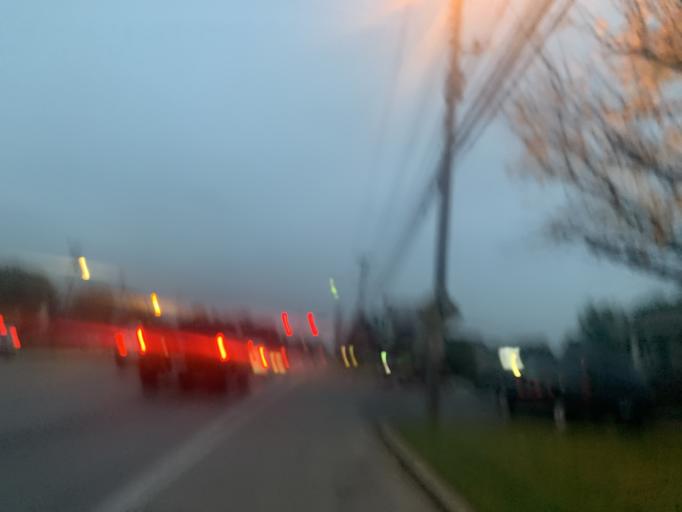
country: US
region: Kentucky
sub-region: Jefferson County
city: Shively
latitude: 38.2160
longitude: -85.7954
